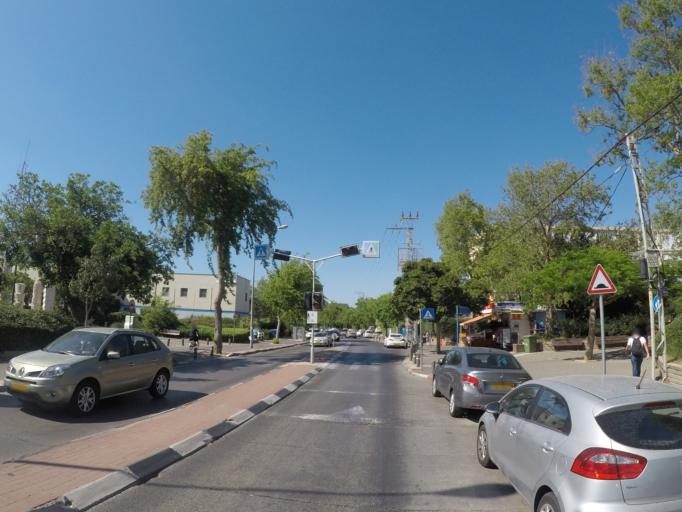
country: IL
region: Tel Aviv
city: Ramat Gan
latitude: 32.1075
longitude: 34.7982
